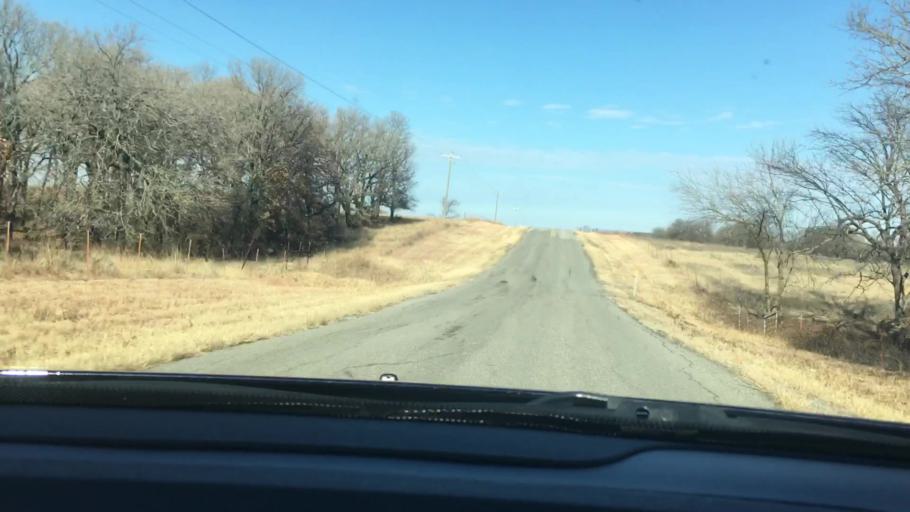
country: US
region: Oklahoma
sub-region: Garvin County
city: Wynnewood
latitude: 34.6709
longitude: -97.1254
